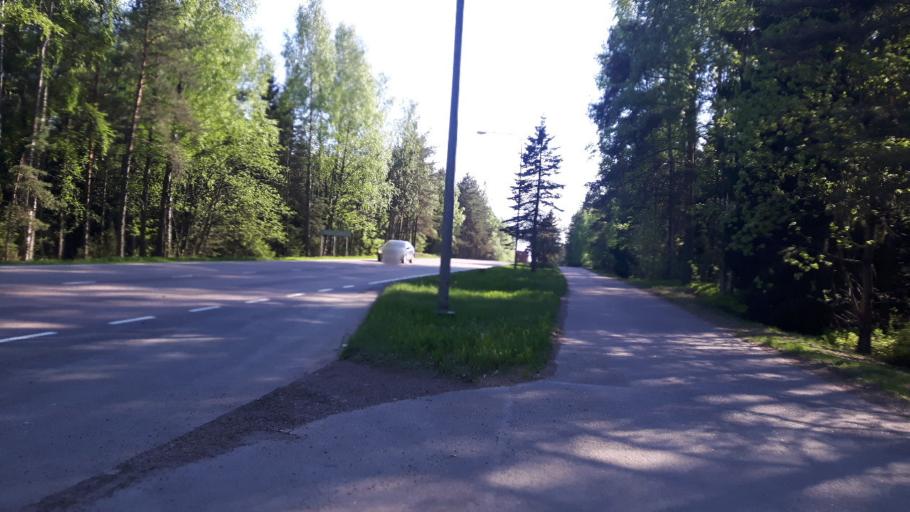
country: FI
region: Kymenlaakso
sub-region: Kotka-Hamina
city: Kotka
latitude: 60.4480
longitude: 26.8940
